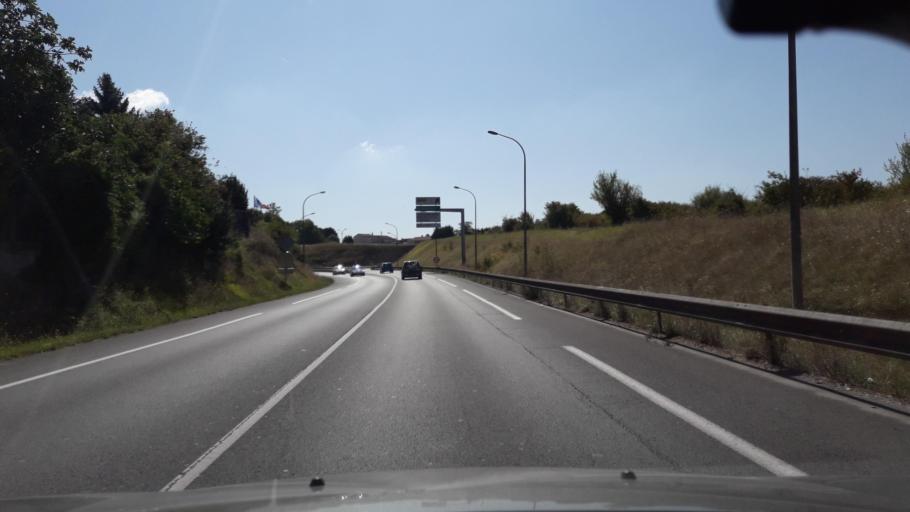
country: FR
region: Poitou-Charentes
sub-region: Departement de la Charente
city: Chateaubernard
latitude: 45.6777
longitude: -0.3312
